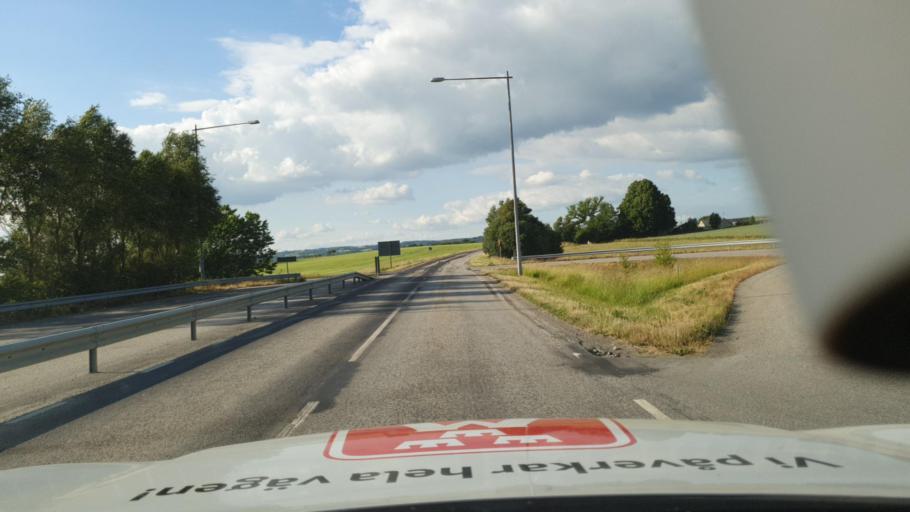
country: SE
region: Skane
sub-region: Skurups Kommun
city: Rydsgard
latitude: 55.4836
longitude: 13.5924
